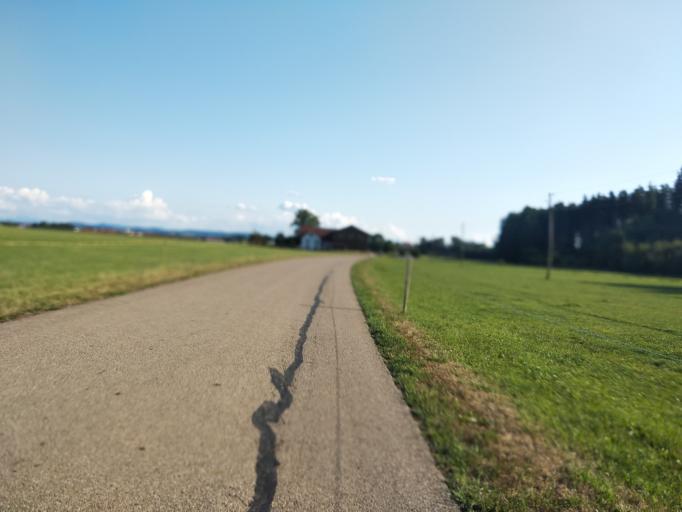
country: DE
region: Bavaria
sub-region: Swabia
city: Lautrach
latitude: 47.8772
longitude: 10.1182
